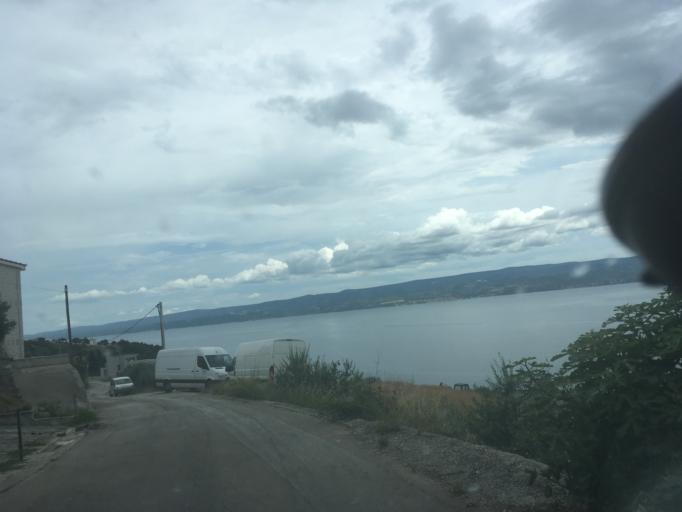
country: HR
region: Splitsko-Dalmatinska
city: Jesenice
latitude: 43.4570
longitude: 16.6208
